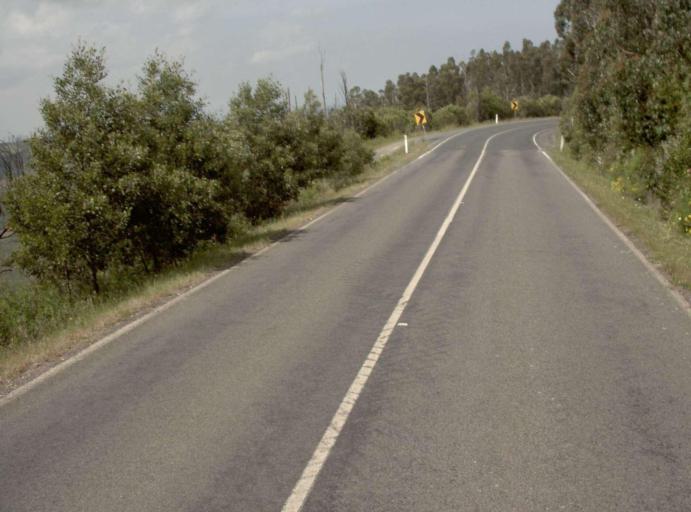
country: AU
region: Victoria
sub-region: Latrobe
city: Traralgon
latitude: -38.3886
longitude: 146.5538
